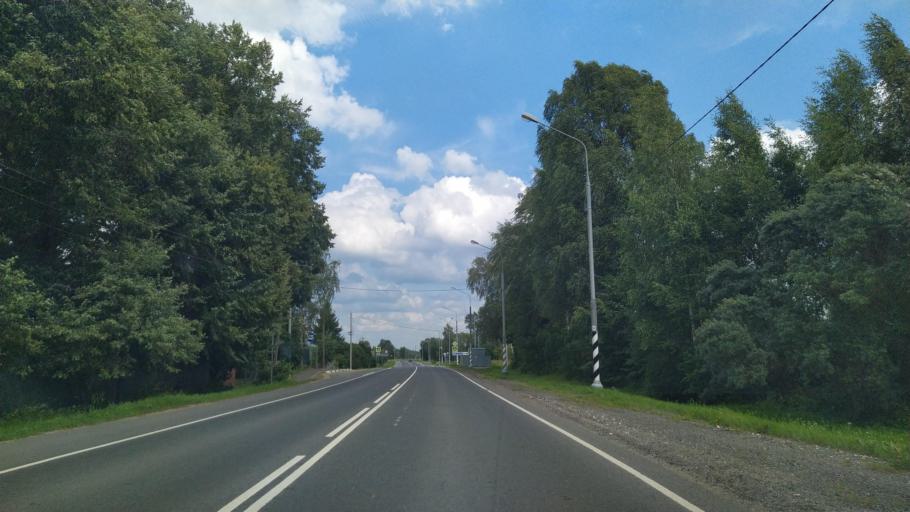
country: RU
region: Pskov
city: Dno
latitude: 58.0613
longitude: 30.0130
